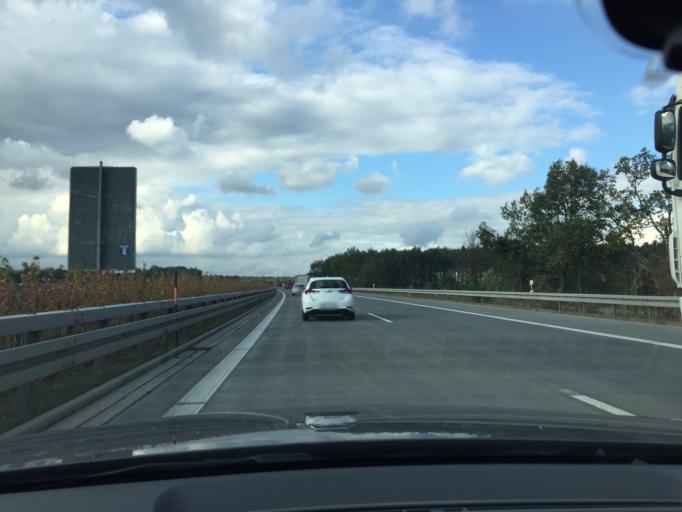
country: DE
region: Brandenburg
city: Lubbenau
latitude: 51.8745
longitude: 13.8920
